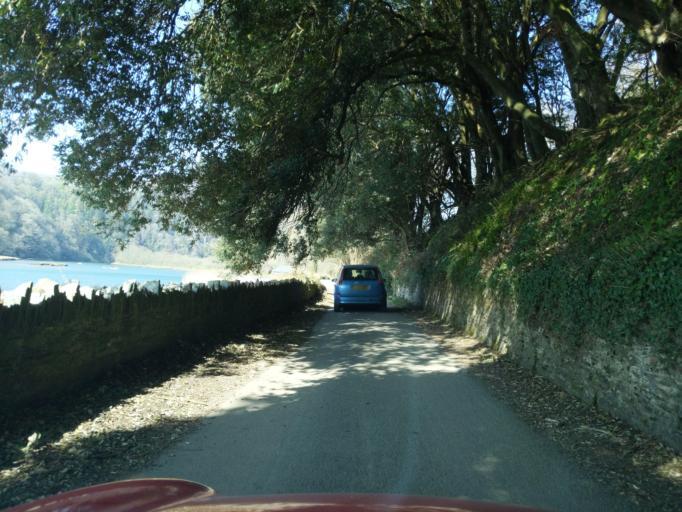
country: GB
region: England
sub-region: Devon
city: Bere Alston
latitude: 50.4569
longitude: -4.1544
